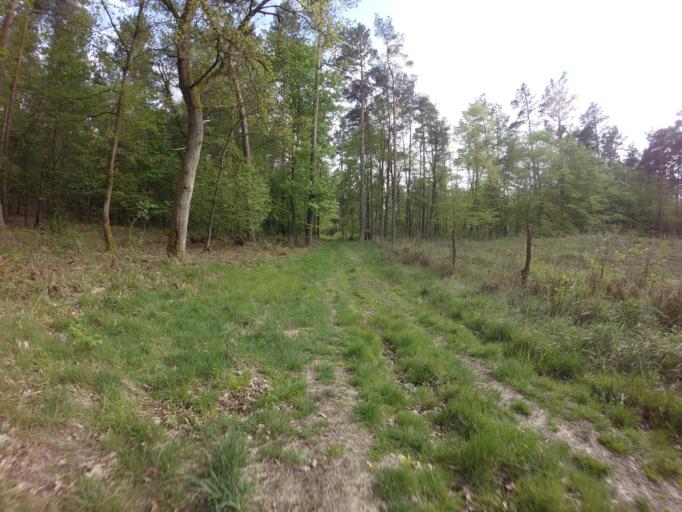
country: PL
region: West Pomeranian Voivodeship
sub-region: Powiat choszczenski
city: Choszczno
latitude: 53.1540
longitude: 15.3286
